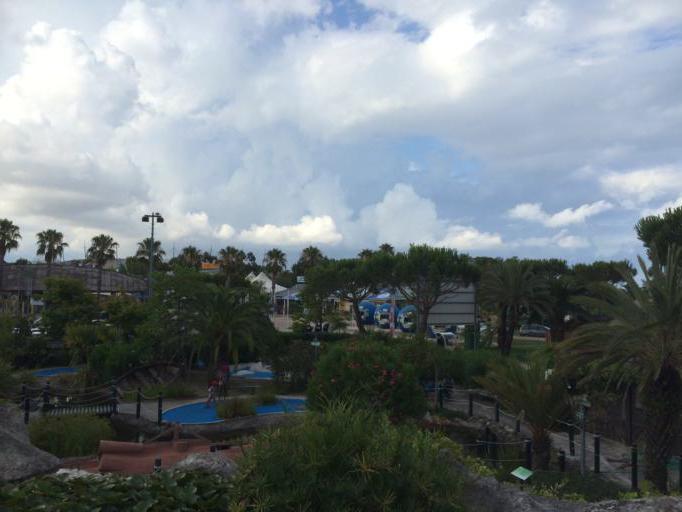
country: FR
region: Provence-Alpes-Cote d'Azur
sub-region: Departement des Alpes-Maritimes
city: Biot
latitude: 43.6136
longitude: 7.1239
